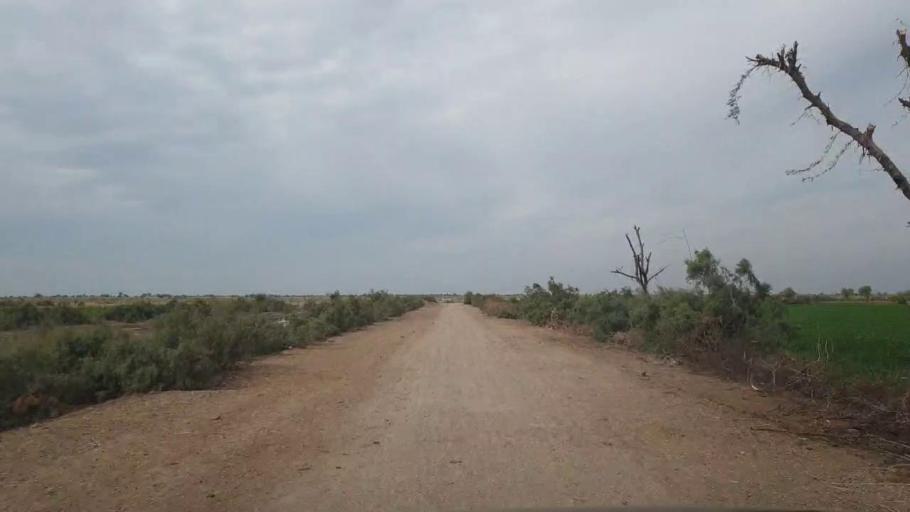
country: PK
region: Sindh
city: Sanghar
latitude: 26.0475
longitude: 68.9056
